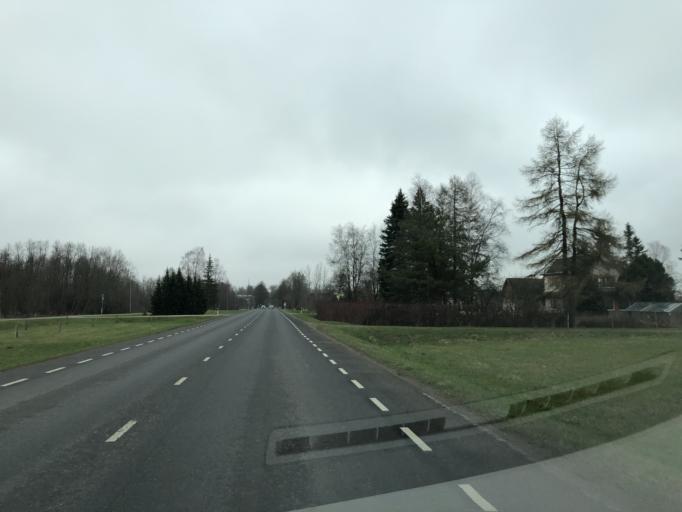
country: EE
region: Laeaene-Virumaa
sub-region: Vaeike-Maarja vald
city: Vaike-Maarja
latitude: 59.1204
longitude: 26.2476
